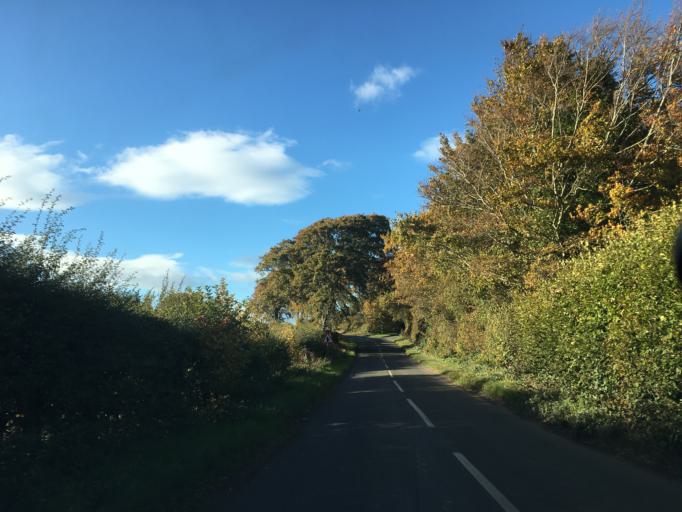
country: GB
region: Scotland
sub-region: East Lothian
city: Pencaitland
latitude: 55.8681
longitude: -2.8903
